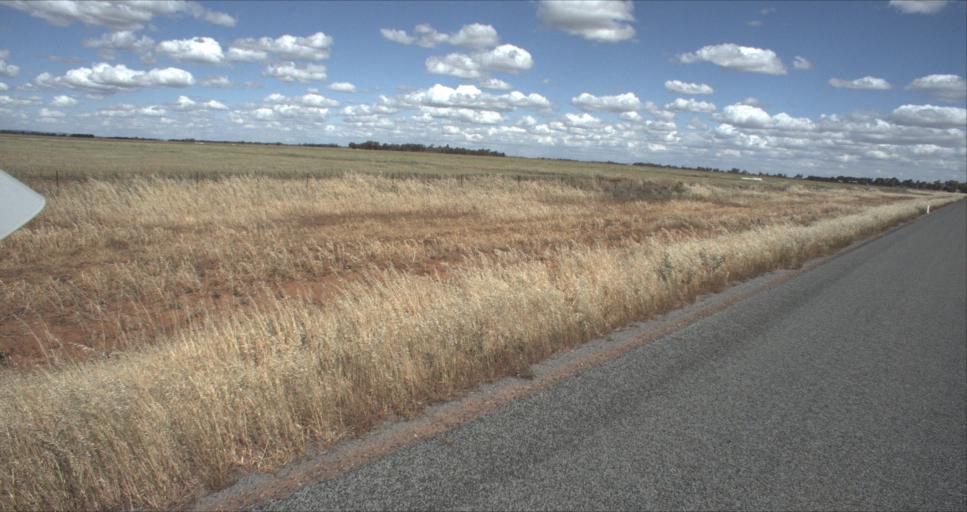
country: AU
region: New South Wales
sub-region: Leeton
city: Leeton
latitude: -34.4633
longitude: 146.2523
